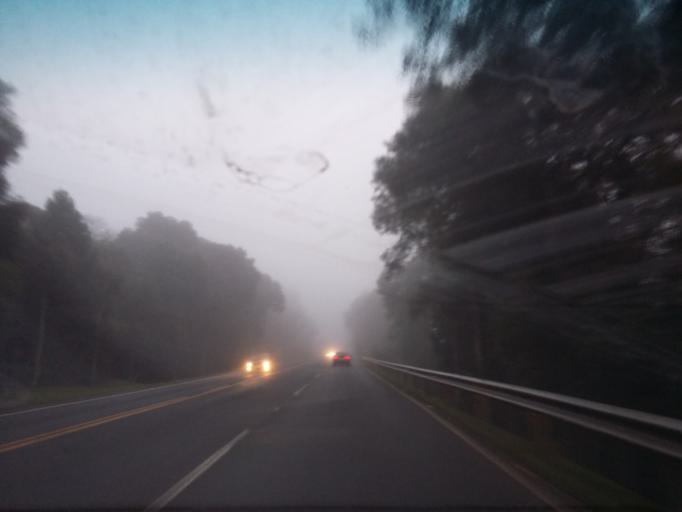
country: BR
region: Santa Catarina
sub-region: Correia Pinto
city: Correia Pinto
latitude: -27.4396
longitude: -50.3979
